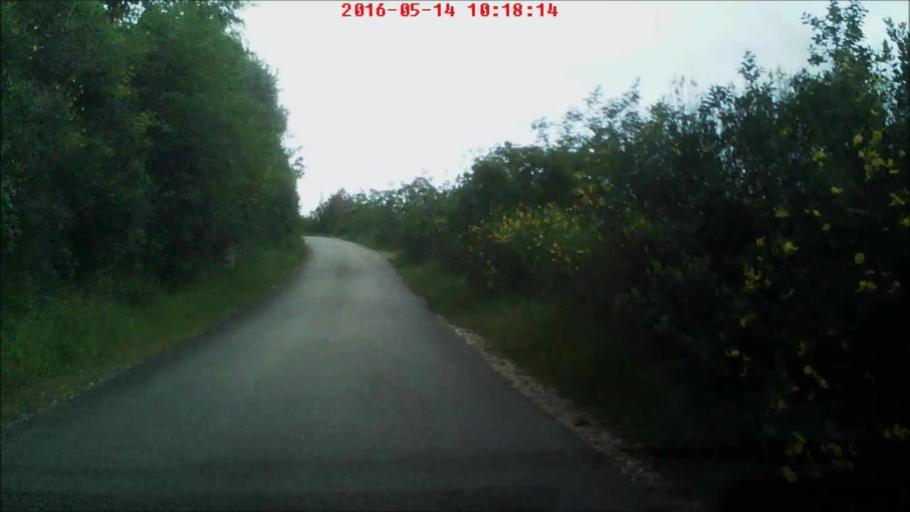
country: HR
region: Dubrovacko-Neretvanska
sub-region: Grad Dubrovnik
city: Mokosica
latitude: 42.7203
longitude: 17.9678
